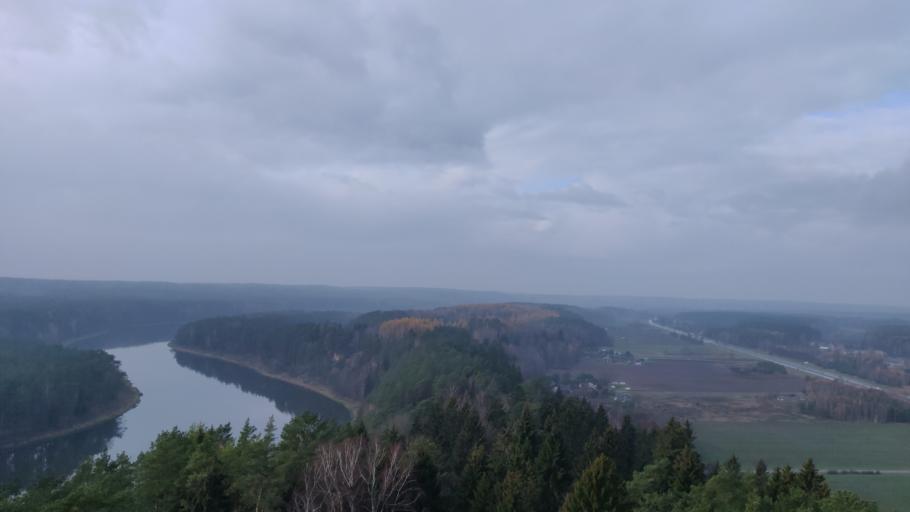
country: LT
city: Birstonas
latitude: 54.6038
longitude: 24.0127
